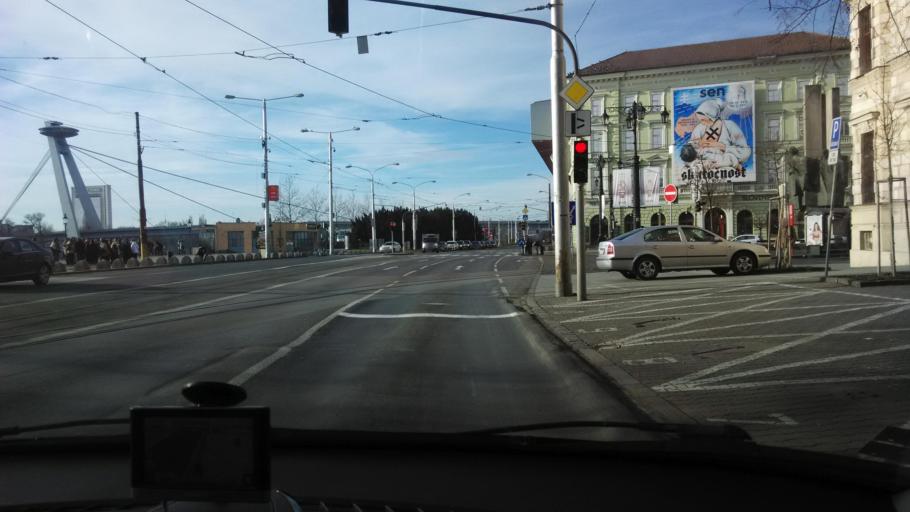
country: SK
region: Bratislavsky
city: Bratislava
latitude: 48.1401
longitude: 17.1106
